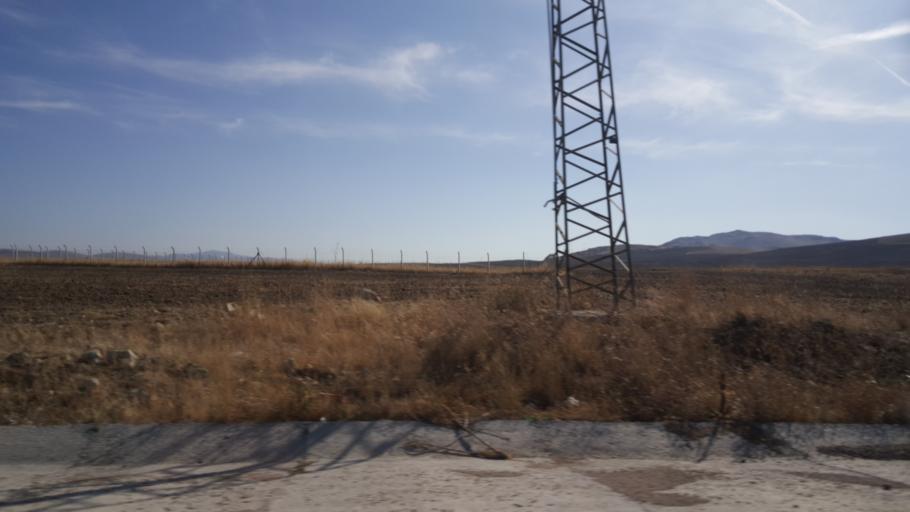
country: TR
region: Ankara
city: Yenice
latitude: 39.3746
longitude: 32.7324
